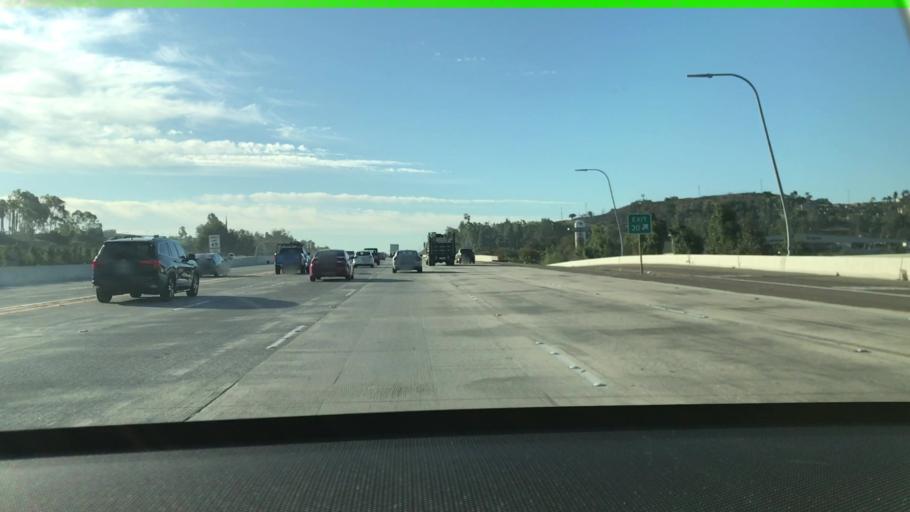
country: US
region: California
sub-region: San Diego County
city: Escondido
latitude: 33.1114
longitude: -117.0970
